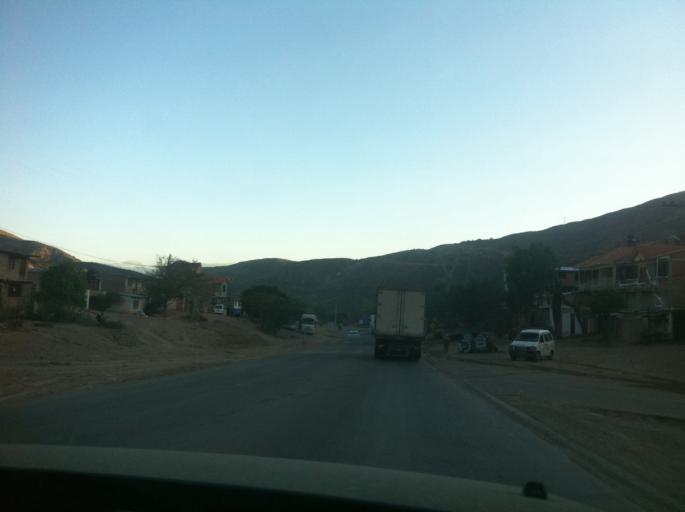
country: BO
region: Cochabamba
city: Sipe Sipe
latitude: -17.5637
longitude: -66.3447
